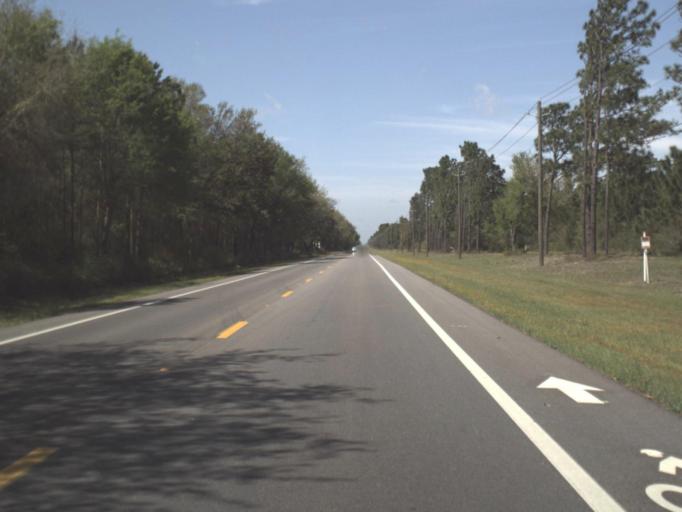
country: US
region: Florida
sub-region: Santa Rosa County
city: East Milton
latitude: 30.6432
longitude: -86.9357
